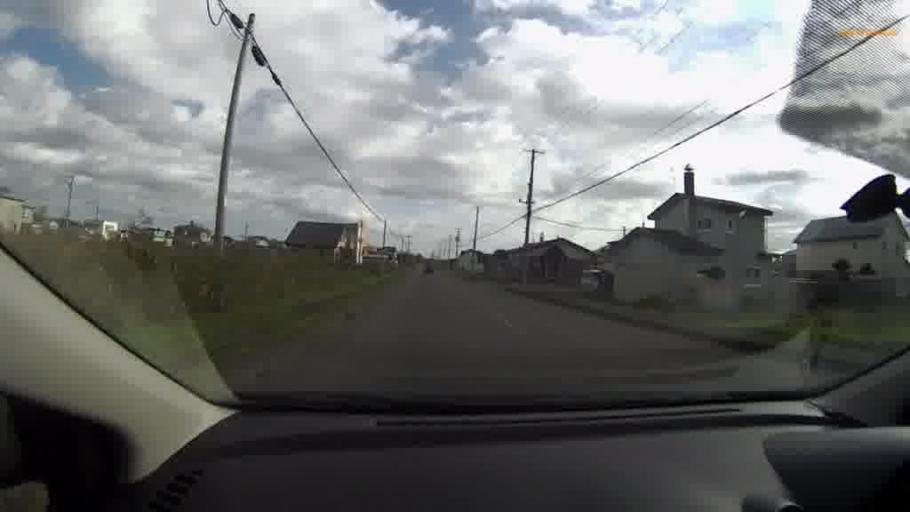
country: JP
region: Hokkaido
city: Kushiro
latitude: 42.9764
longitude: 144.1243
